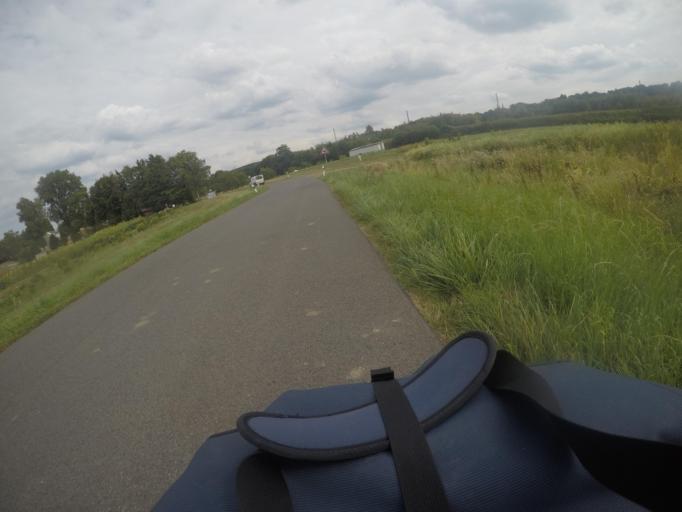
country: DE
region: North Rhine-Westphalia
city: Haan
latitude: 51.2206
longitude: 7.0425
